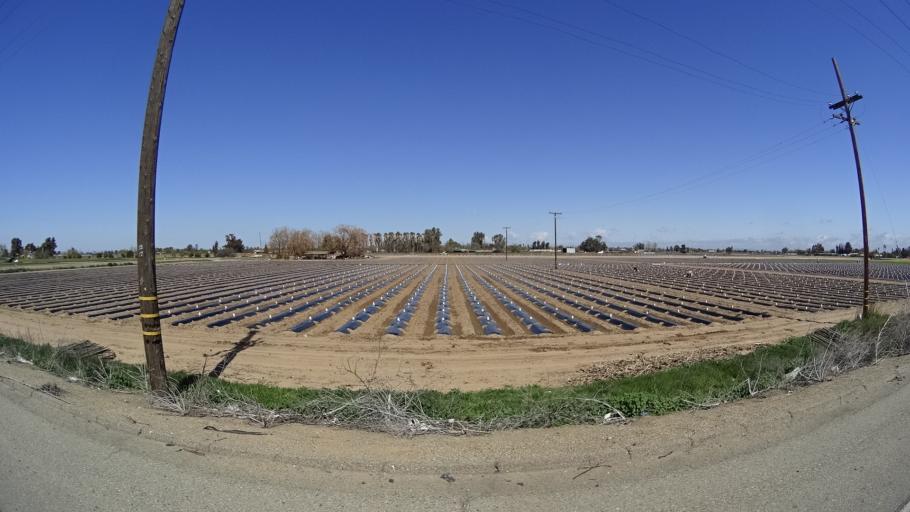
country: US
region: California
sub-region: Fresno County
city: West Park
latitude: 36.7065
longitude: -119.8612
